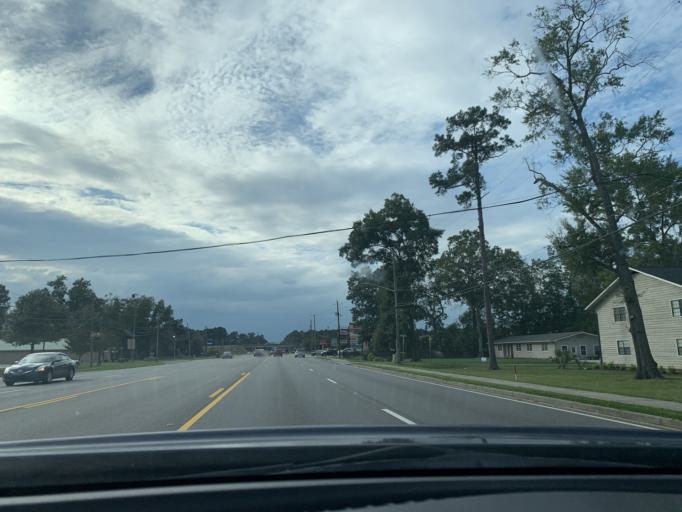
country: US
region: Georgia
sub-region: Chatham County
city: Pooler
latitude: 32.1208
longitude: -81.2626
